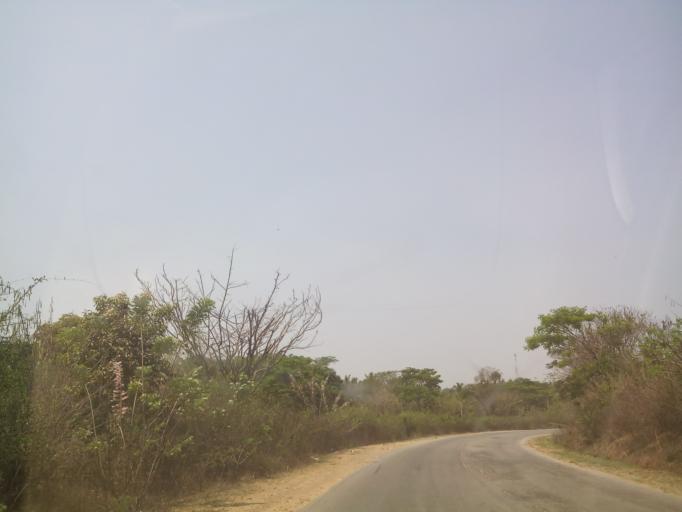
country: IN
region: Karnataka
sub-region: Hassan
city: Alur
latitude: 12.9816
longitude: 76.0403
